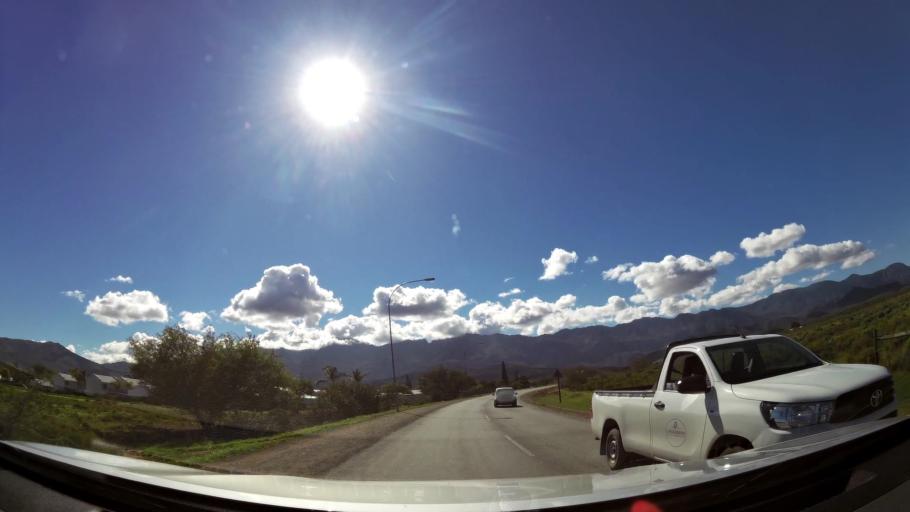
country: ZA
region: Western Cape
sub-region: Cape Winelands District Municipality
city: Ashton
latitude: -33.8117
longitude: 19.8975
